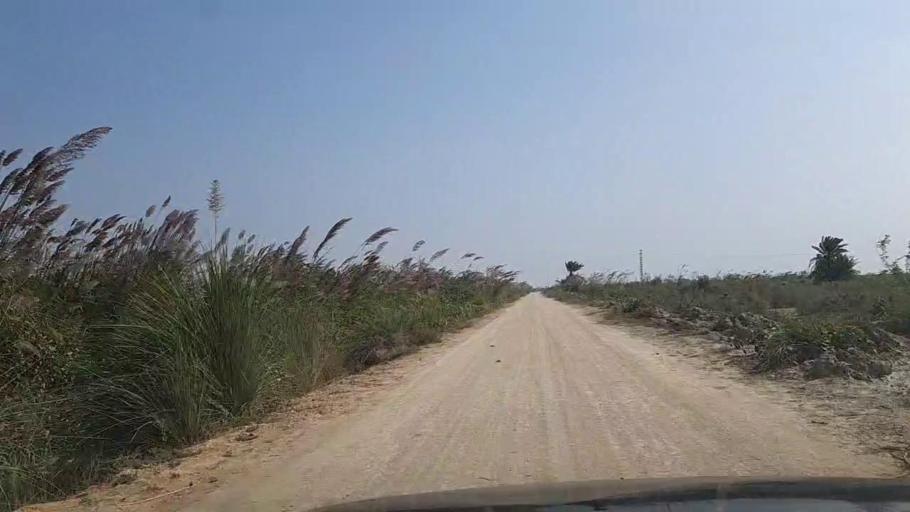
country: PK
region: Sindh
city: Gharo
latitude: 24.7199
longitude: 67.5594
